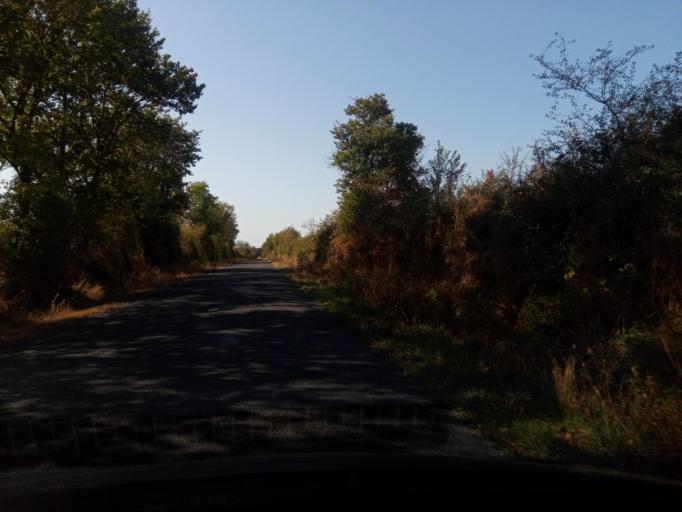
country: FR
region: Poitou-Charentes
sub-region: Departement de la Vienne
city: Saulge
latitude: 46.3602
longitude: 0.8768
